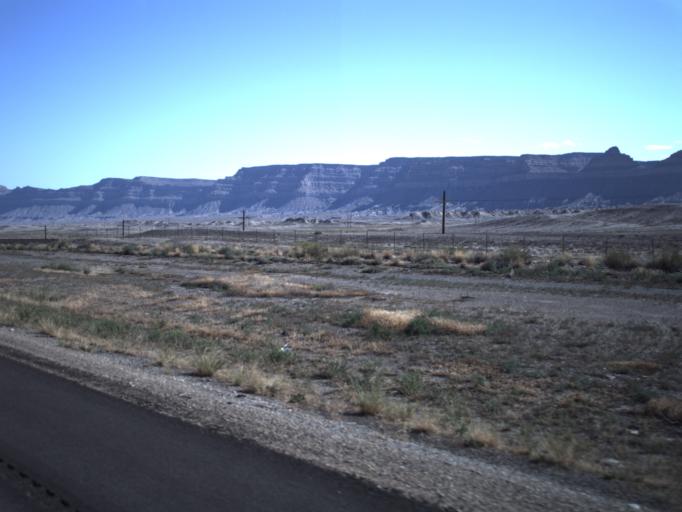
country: US
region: Utah
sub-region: Carbon County
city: East Carbon City
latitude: 39.0591
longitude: -110.3124
